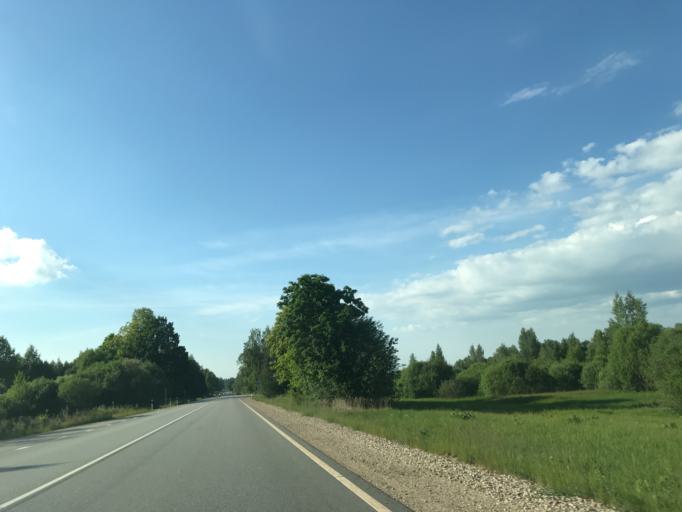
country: LV
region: Ogre
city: Jumprava
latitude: 56.6435
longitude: 24.8849
